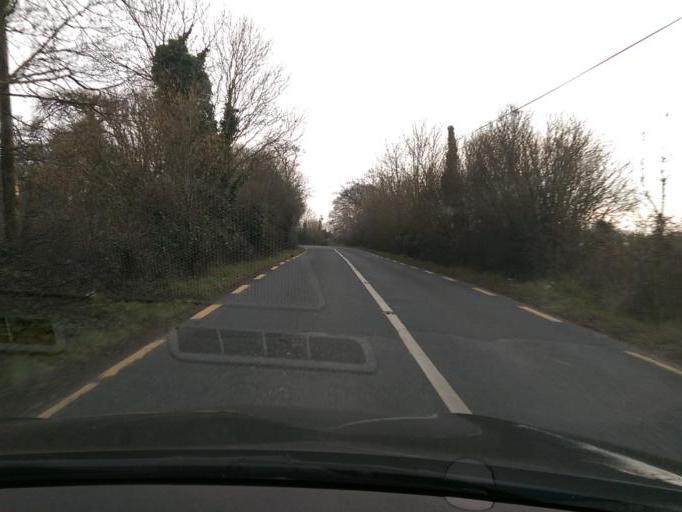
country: IE
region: Leinster
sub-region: An Iarmhi
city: Athlone
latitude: 53.4604
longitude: -7.8764
